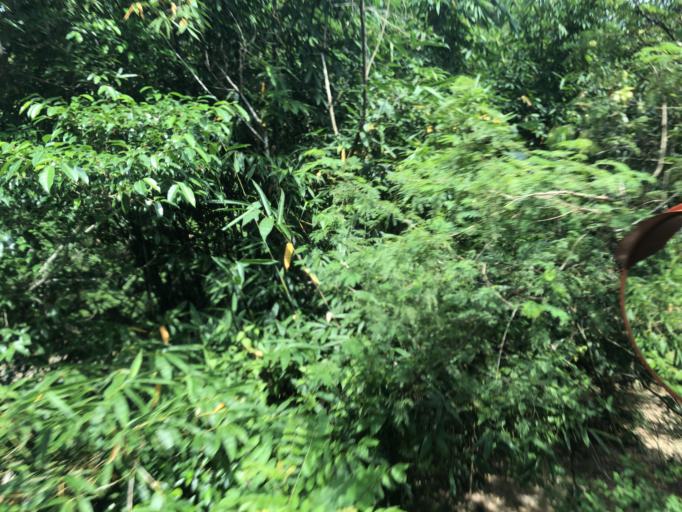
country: TW
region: Taiwan
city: Yujing
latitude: 22.9331
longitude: 120.5906
